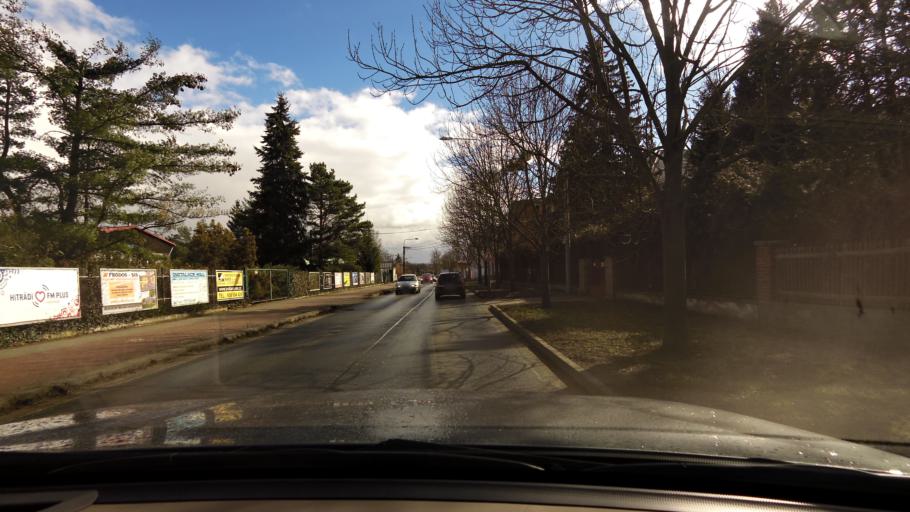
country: CZ
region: Plzensky
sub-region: Okres Plzen-Mesto
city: Pilsen
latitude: 49.7720
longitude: 13.3955
